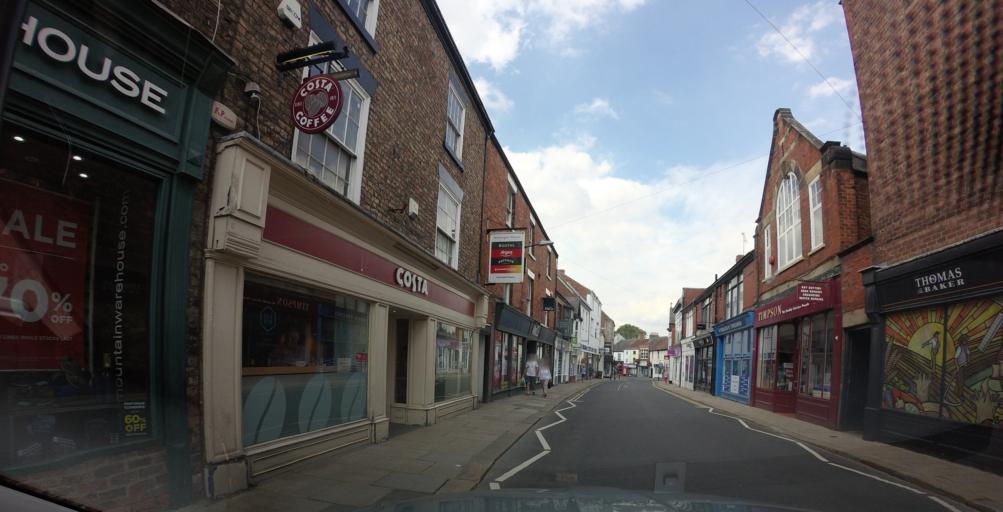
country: GB
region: England
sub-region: North Yorkshire
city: Ripon
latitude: 54.1368
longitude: -1.5240
